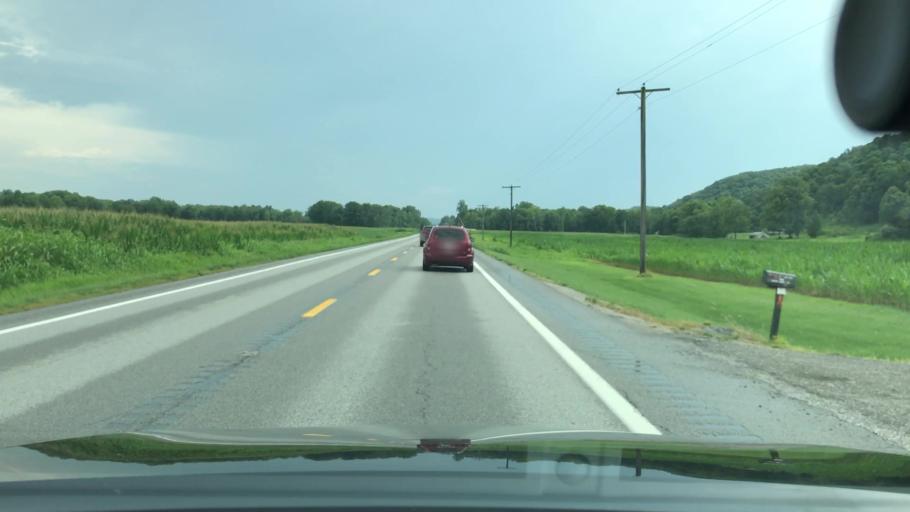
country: US
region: West Virginia
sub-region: Putnam County
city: Buffalo
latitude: 38.6972
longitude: -81.9660
